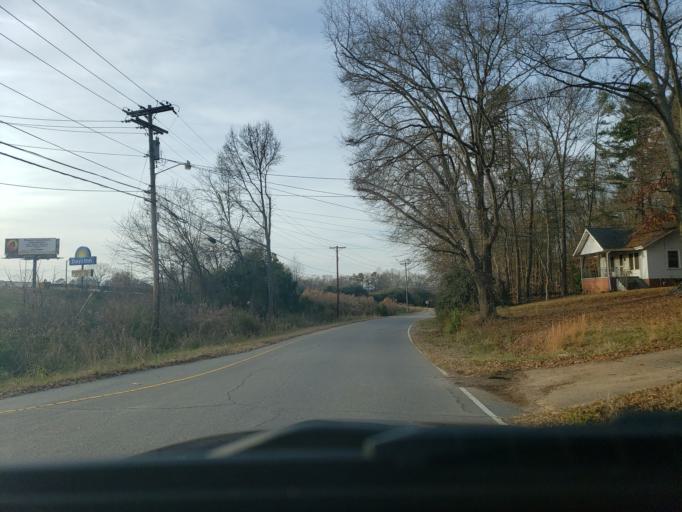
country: US
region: North Carolina
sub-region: Cleveland County
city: Shelby
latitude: 35.2900
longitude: -81.5632
